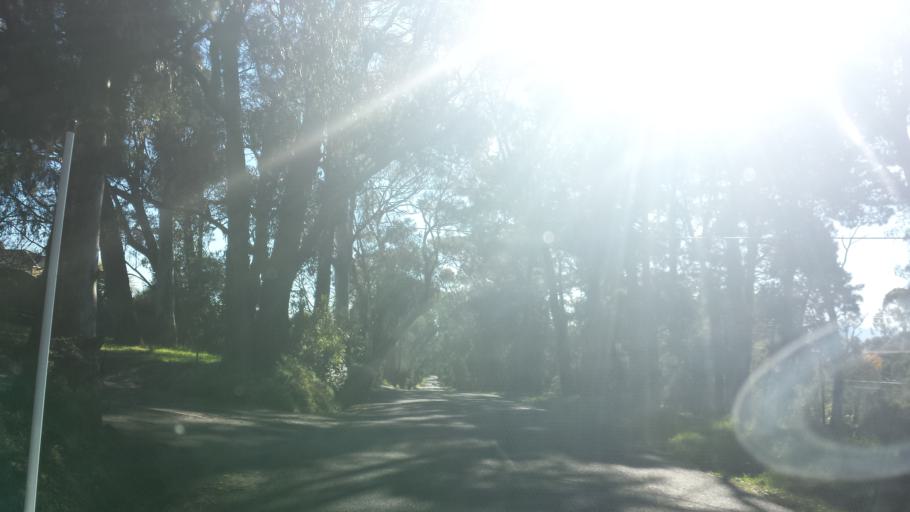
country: AU
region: Victoria
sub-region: Yarra Ranges
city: Lilydale
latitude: -37.7592
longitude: 145.3720
